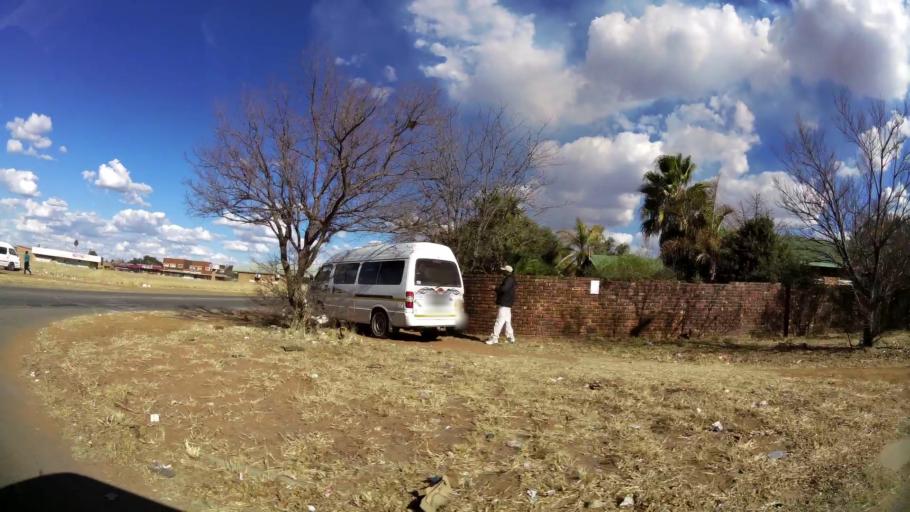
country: ZA
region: North-West
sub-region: Dr Kenneth Kaunda District Municipality
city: Klerksdorp
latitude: -26.8243
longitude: 26.6572
